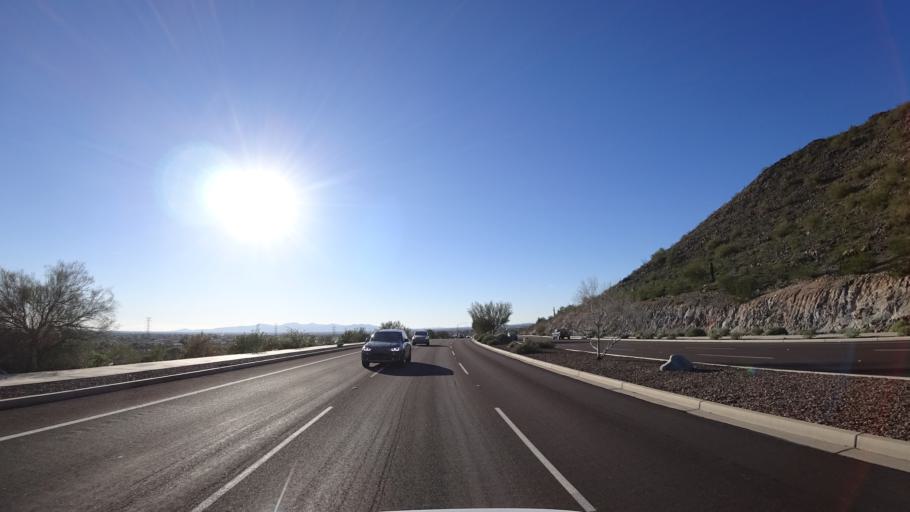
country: US
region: Arizona
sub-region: Maricopa County
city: Sun City West
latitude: 33.7107
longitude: -112.2517
